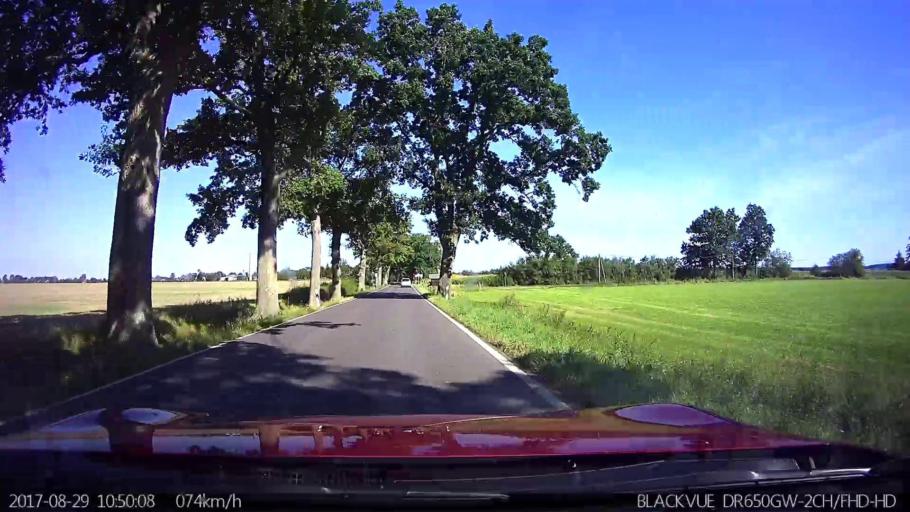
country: DE
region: Mecklenburg-Vorpommern
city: Velgast
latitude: 54.2563
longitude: 12.8218
